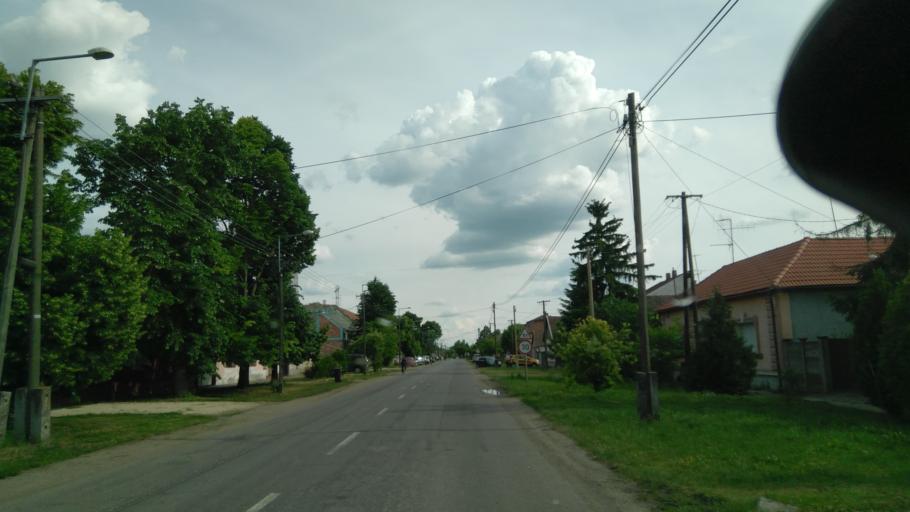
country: HU
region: Bekes
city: Battonya
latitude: 46.2887
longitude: 21.0172
